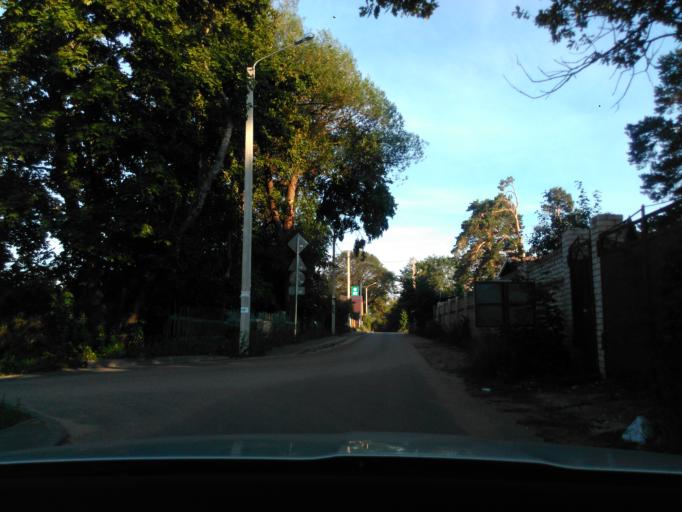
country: RU
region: Tverskaya
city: Konakovo
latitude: 56.7572
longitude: 36.7485
